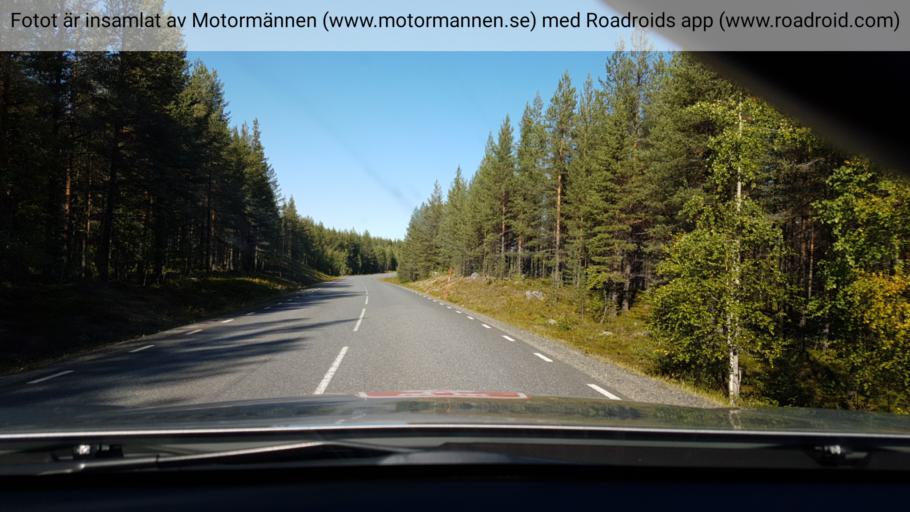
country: SE
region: Vaesterbotten
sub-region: Norsjo Kommun
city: Norsjoe
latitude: 64.9963
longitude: 19.4284
